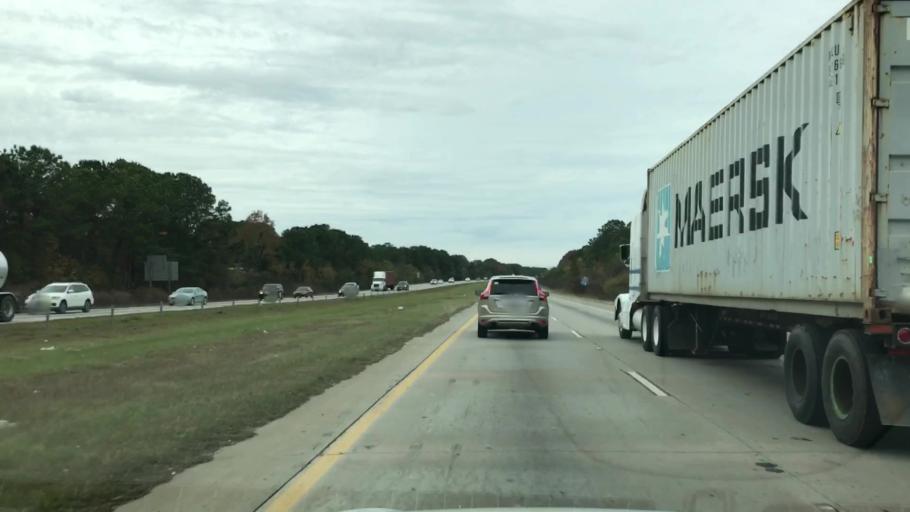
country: US
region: South Carolina
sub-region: Charleston County
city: Mount Pleasant
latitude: 32.8437
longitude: -79.8702
